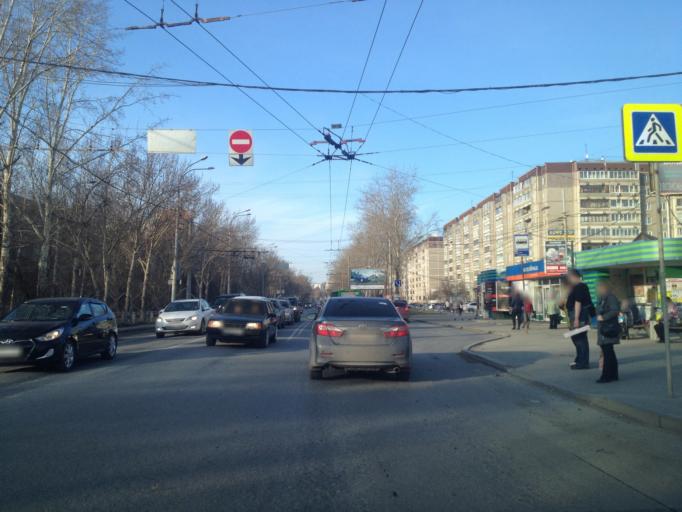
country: RU
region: Sverdlovsk
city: Sovkhoznyy
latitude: 56.7974
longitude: 60.5803
